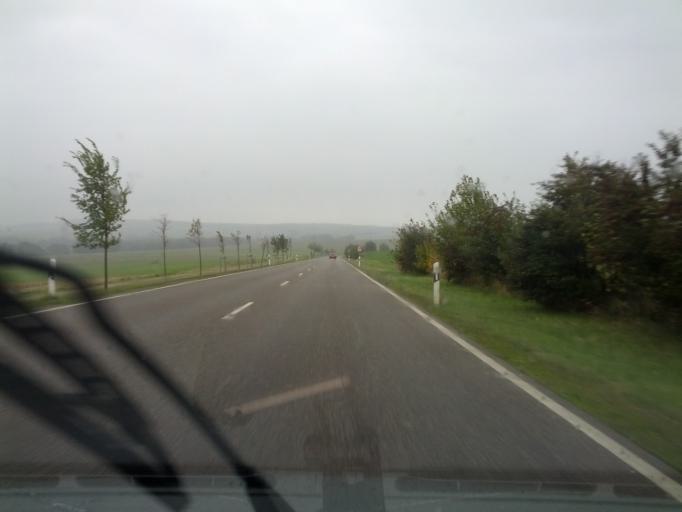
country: DE
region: Saxony
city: Hartenstein
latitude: 50.6826
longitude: 12.7031
